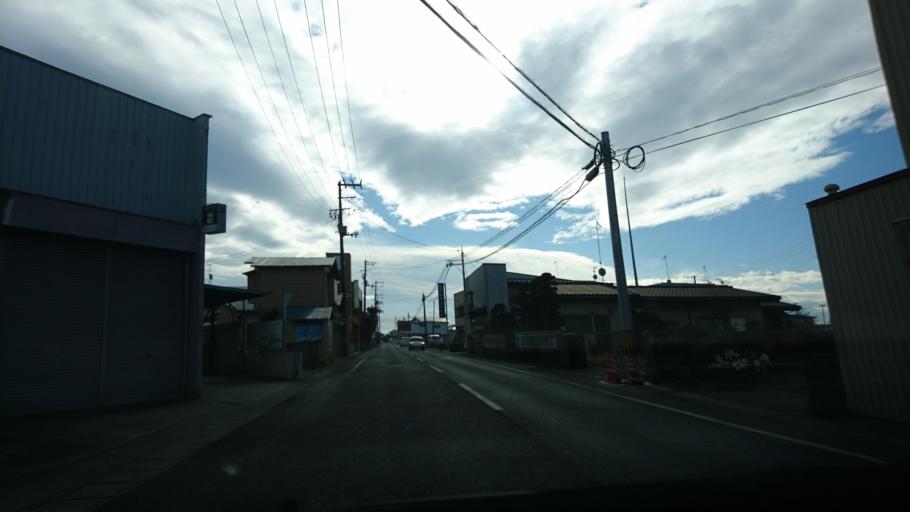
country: JP
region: Miyagi
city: Wakuya
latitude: 38.6840
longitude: 141.1963
